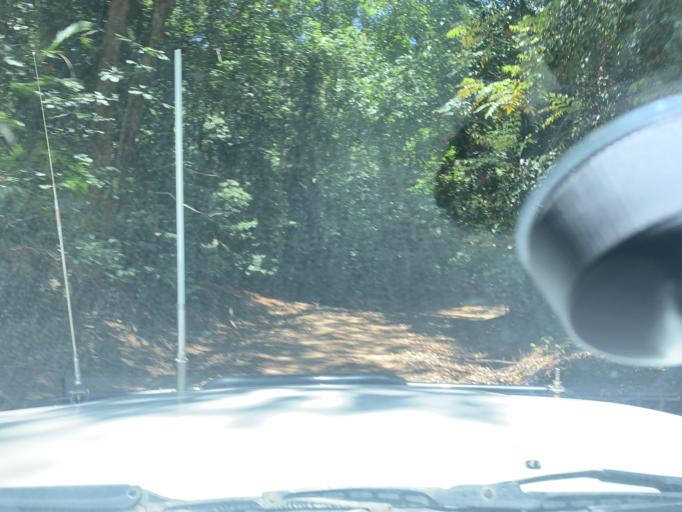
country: AU
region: Queensland
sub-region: Cairns
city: Redlynch
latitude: -16.9711
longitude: 145.6498
